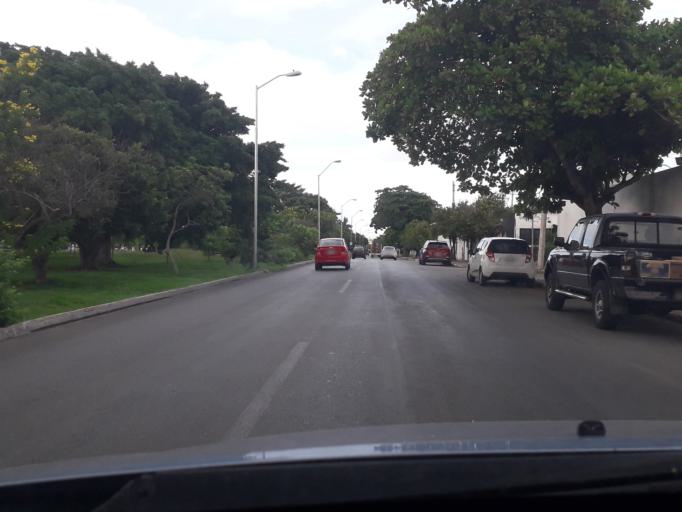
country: MX
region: Yucatan
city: Merida
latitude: 20.9836
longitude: -89.6633
